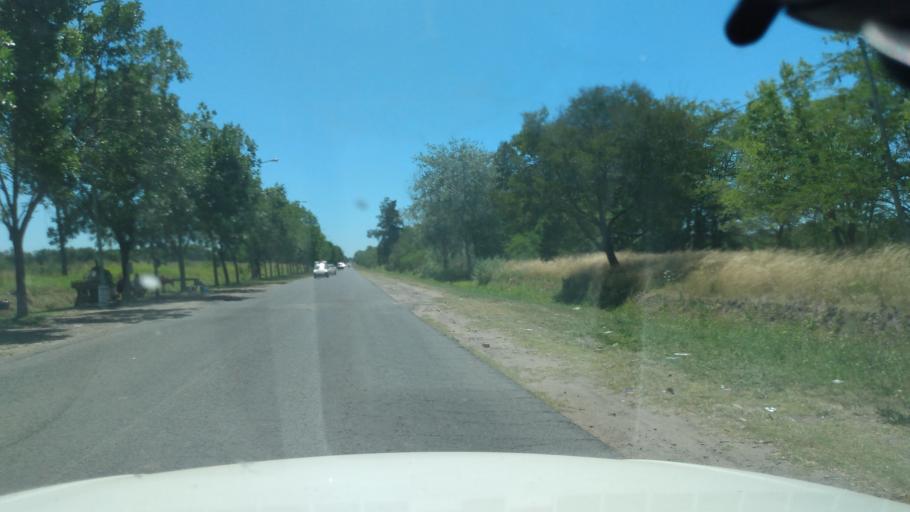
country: AR
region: Buenos Aires
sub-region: Partido de Lujan
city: Lujan
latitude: -34.5789
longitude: -59.1695
